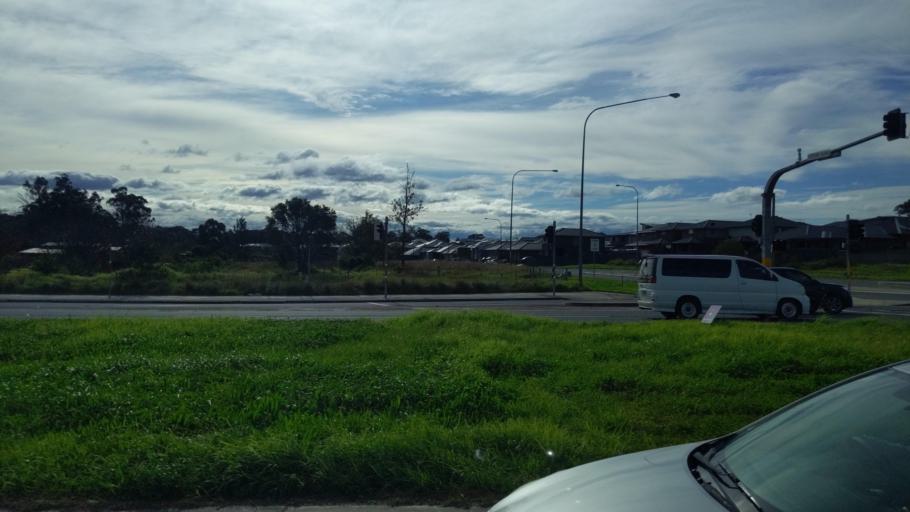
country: AU
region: New South Wales
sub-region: Blacktown
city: Riverstone
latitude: -33.7044
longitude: 150.8661
